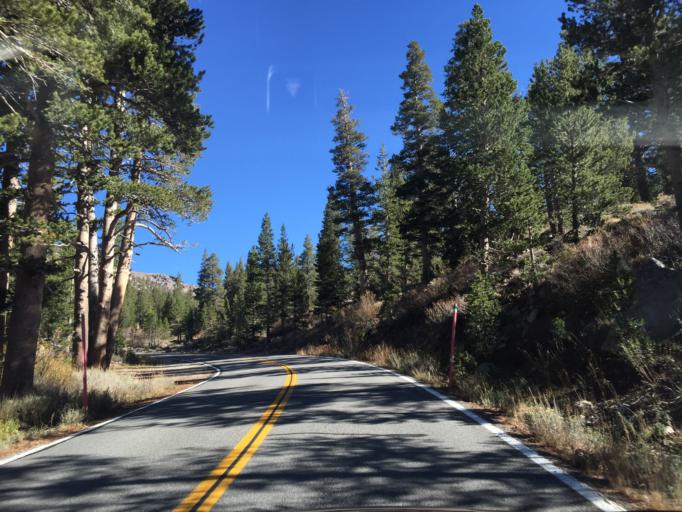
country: US
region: California
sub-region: Mono County
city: Bridgeport
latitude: 38.3250
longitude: -119.6147
